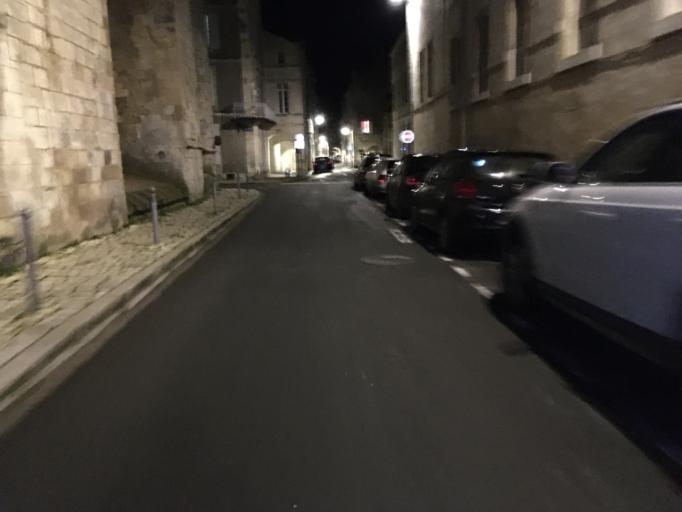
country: FR
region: Poitou-Charentes
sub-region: Departement de la Charente-Maritime
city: La Rochelle
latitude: 46.1612
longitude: -1.1538
